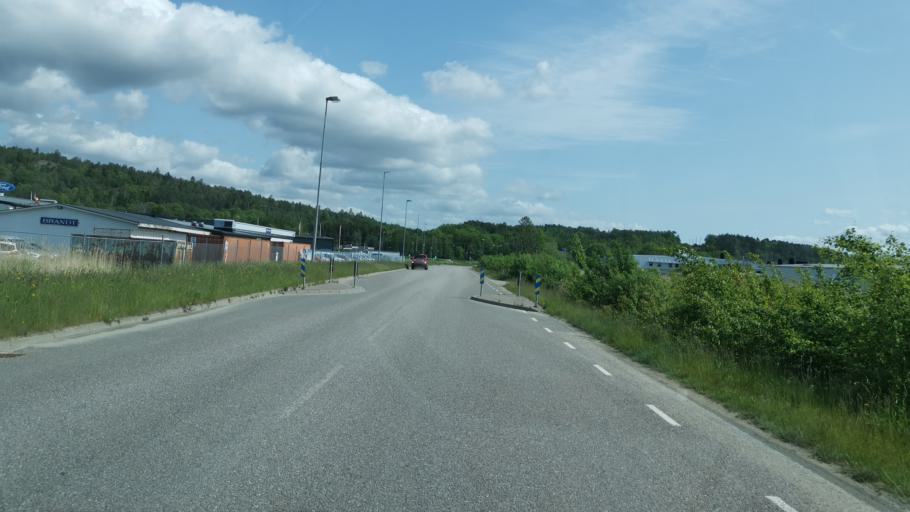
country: SE
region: Vaestra Goetaland
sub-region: Uddevalla Kommun
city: Uddevalla
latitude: 58.3489
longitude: 11.8651
